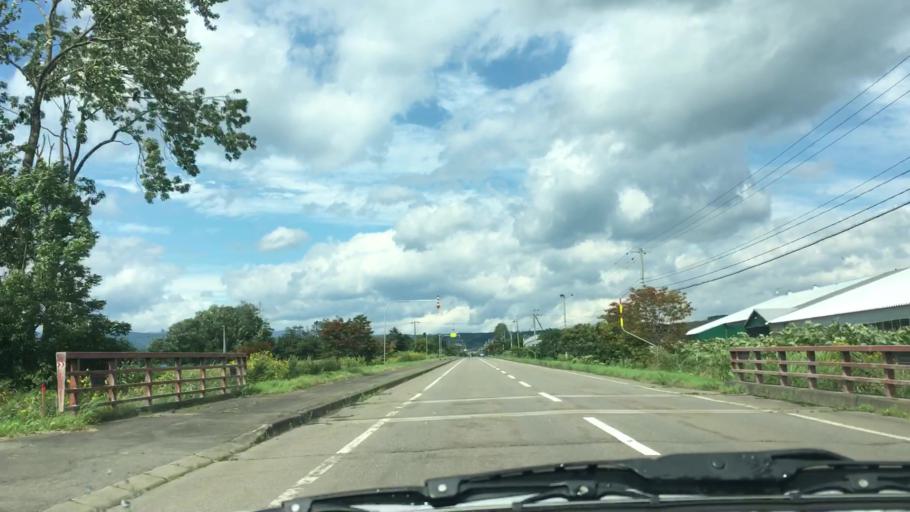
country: JP
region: Hokkaido
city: Otofuke
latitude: 43.2873
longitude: 143.3074
